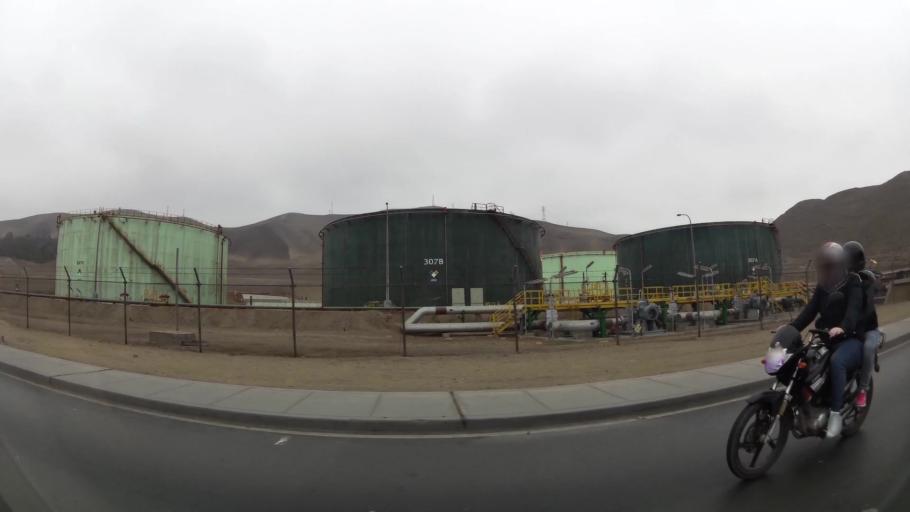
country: PE
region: Lima
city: Ventanilla
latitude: -11.9250
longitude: -77.1294
